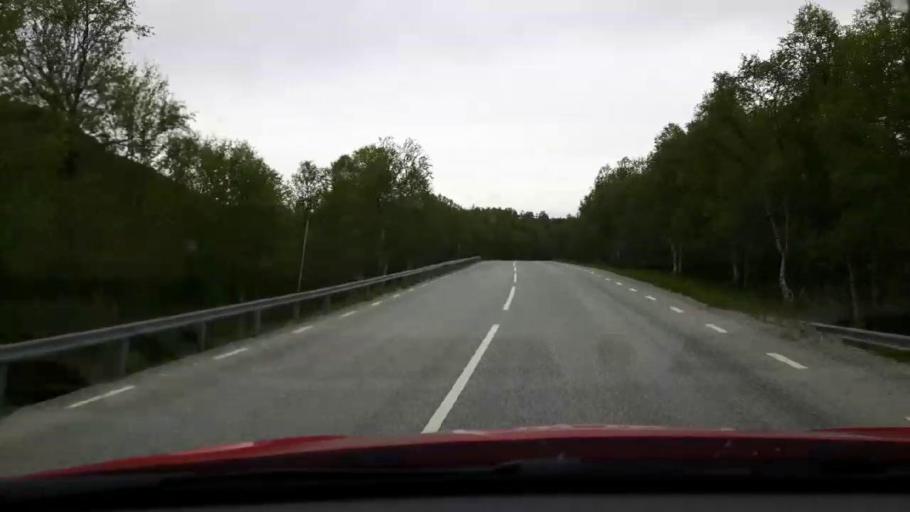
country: NO
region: Sor-Trondelag
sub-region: Tydal
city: Aas
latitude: 62.6841
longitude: 12.4128
